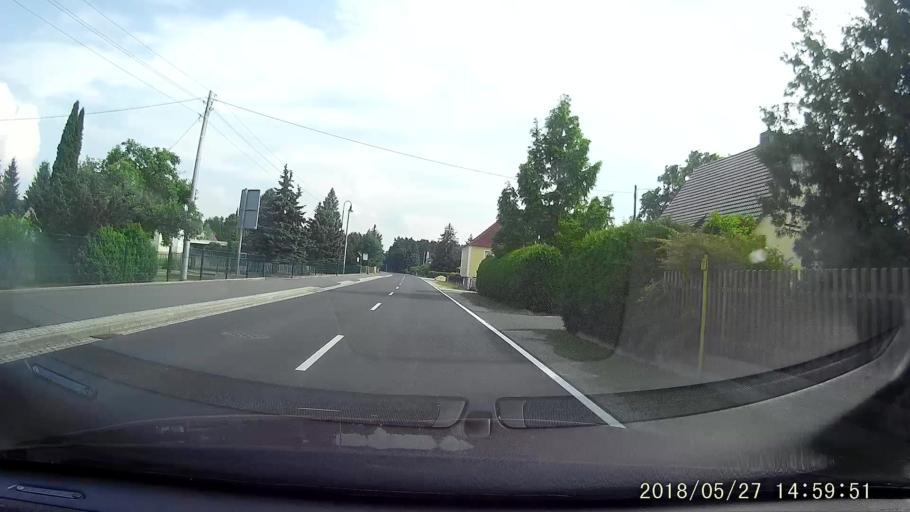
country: DE
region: Saxony
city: Mucka
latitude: 51.3449
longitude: 14.6849
